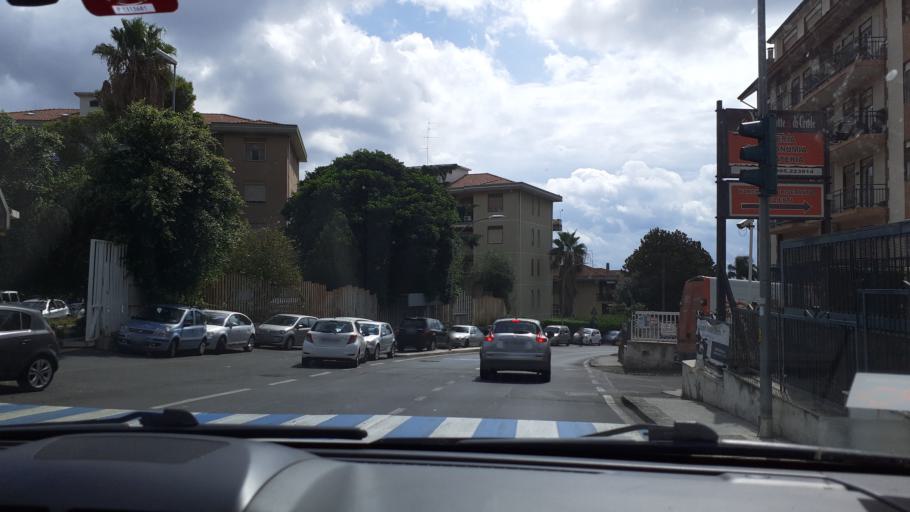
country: IT
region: Sicily
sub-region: Catania
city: Canalicchio
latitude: 37.5389
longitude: 15.0956
